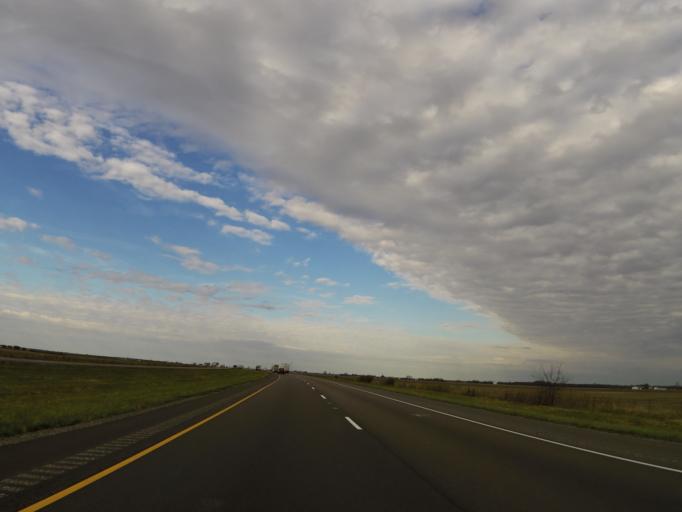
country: US
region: Illinois
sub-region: Washington County
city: Okawville
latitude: 38.4250
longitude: -89.4586
